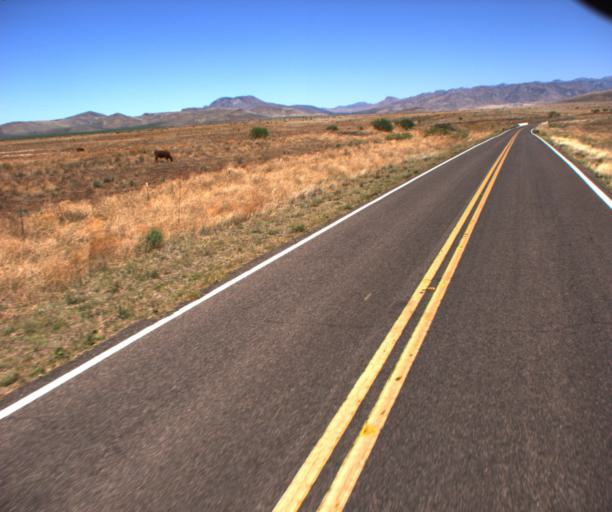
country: US
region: Arizona
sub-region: Cochise County
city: Douglas
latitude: 31.5597
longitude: -109.2652
